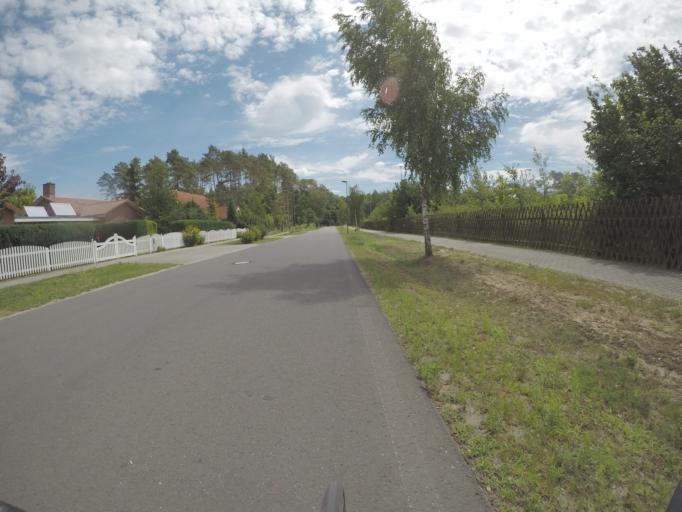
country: DE
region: Brandenburg
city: Storkow
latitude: 52.2456
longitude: 13.9532
